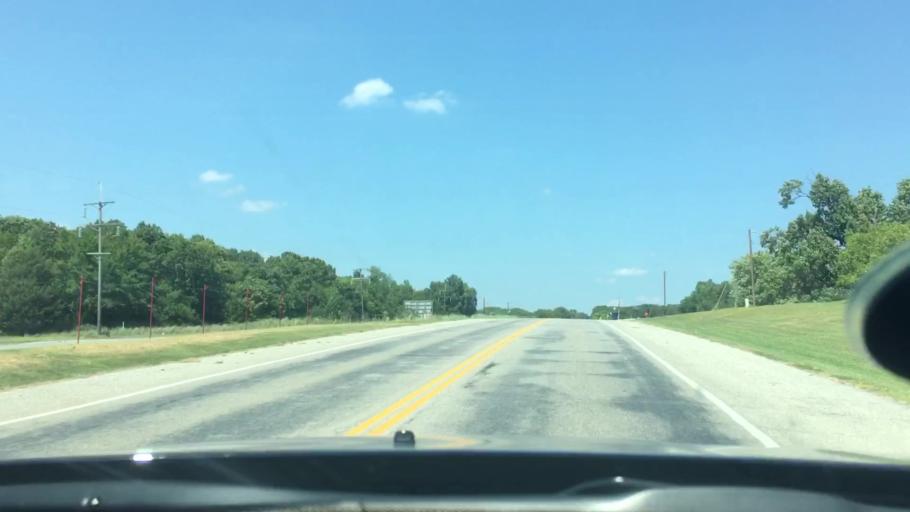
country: US
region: Oklahoma
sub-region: Pontotoc County
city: Byng
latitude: 34.8443
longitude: -96.6785
